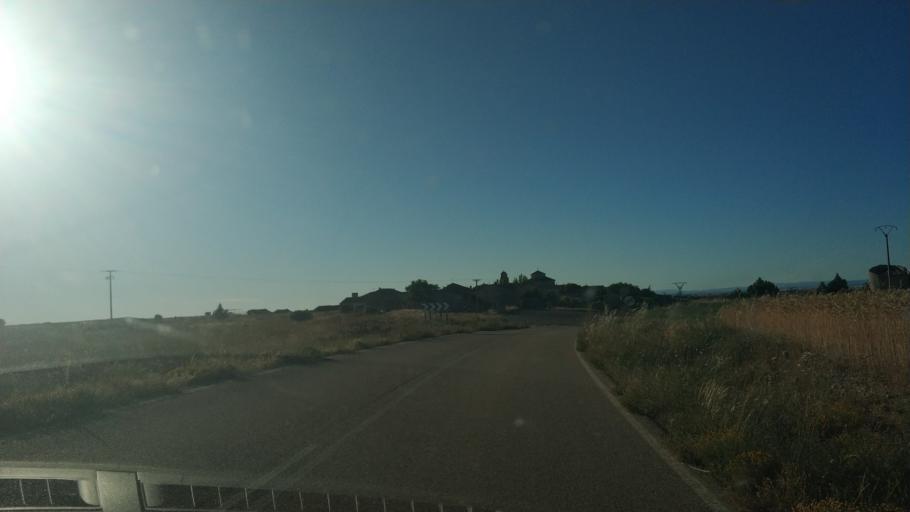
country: ES
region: Castille and Leon
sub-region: Provincia de Soria
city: Liceras
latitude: 41.4613
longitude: -3.2135
